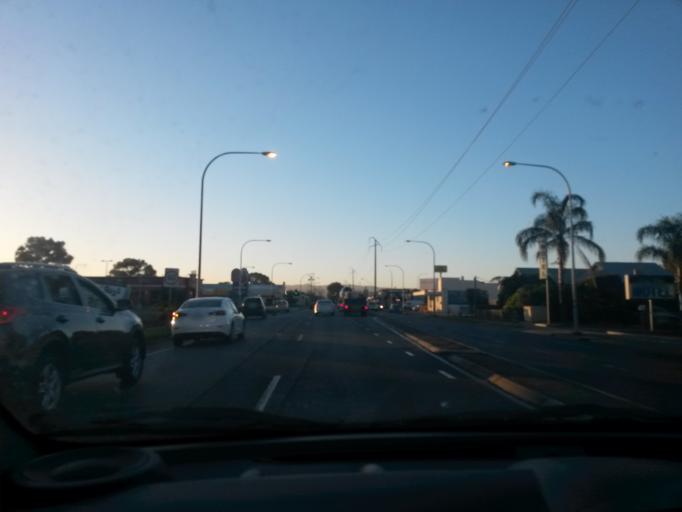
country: AU
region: South Australia
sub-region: Charles Sturt
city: Woodville
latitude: -34.8759
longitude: 138.5497
